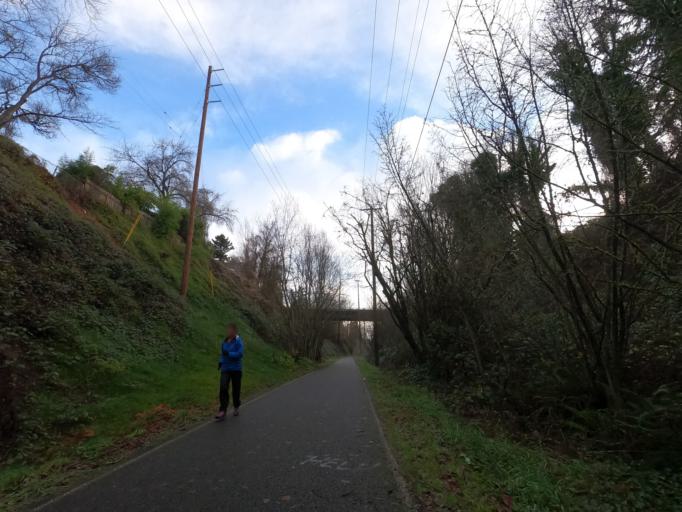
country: US
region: Oregon
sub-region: Clackamas County
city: Milwaukie
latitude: 45.4625
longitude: -122.6316
